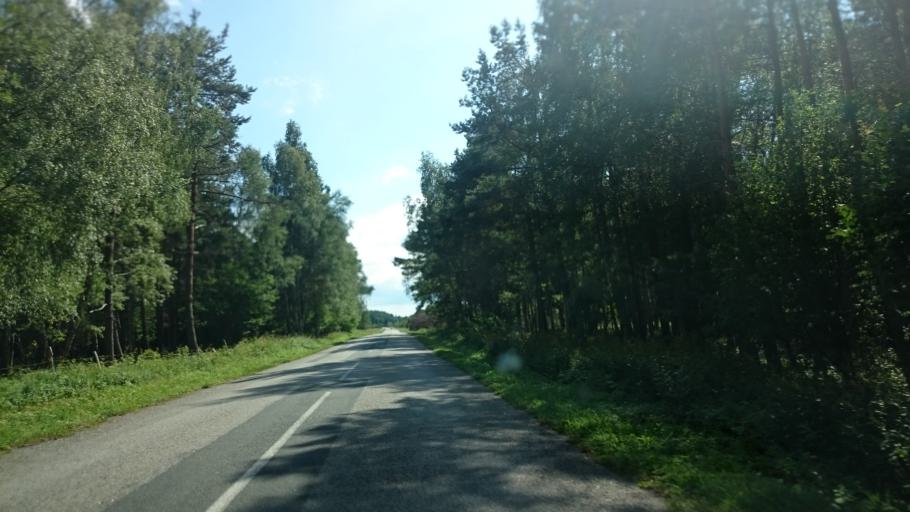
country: EE
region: Saare
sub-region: Orissaare vald
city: Orissaare
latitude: 58.5794
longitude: 22.7649
